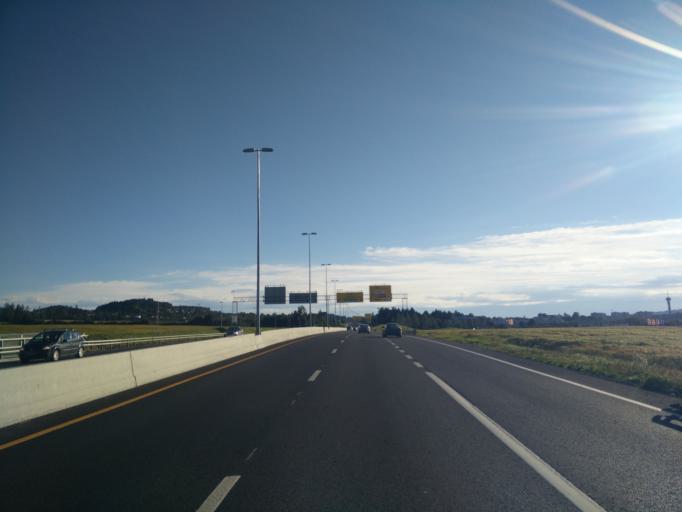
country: NO
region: Sor-Trondelag
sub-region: Trondheim
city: Trondheim
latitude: 63.4293
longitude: 10.4836
